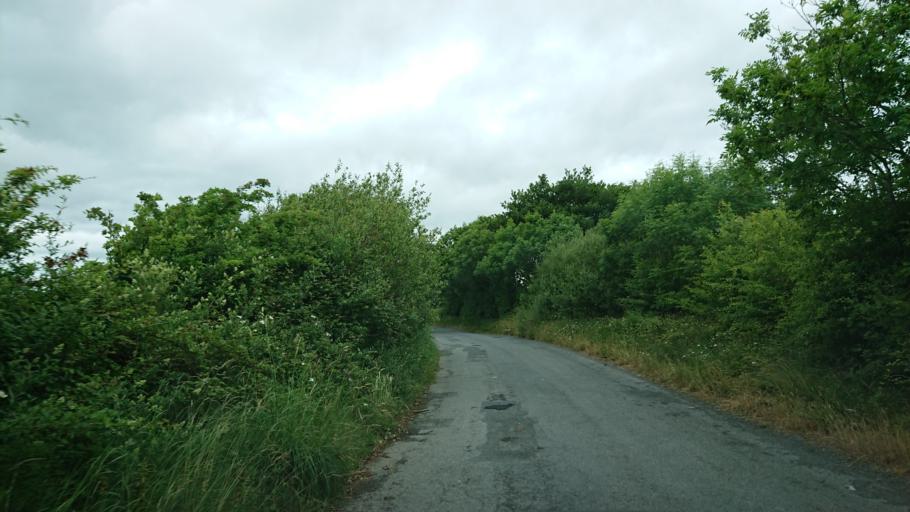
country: IE
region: Munster
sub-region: Waterford
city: Waterford
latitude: 52.2228
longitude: -7.1442
